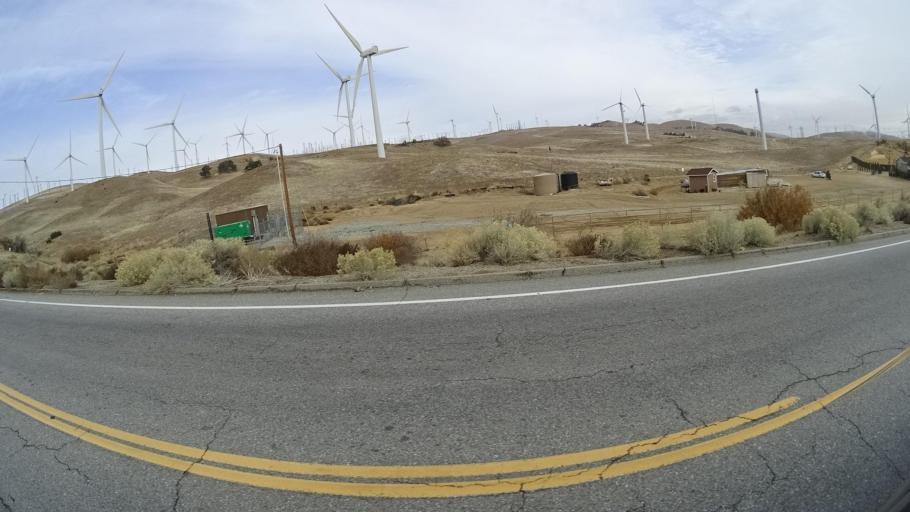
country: US
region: California
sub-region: Kern County
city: Tehachapi
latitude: 35.0556
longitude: -118.3740
